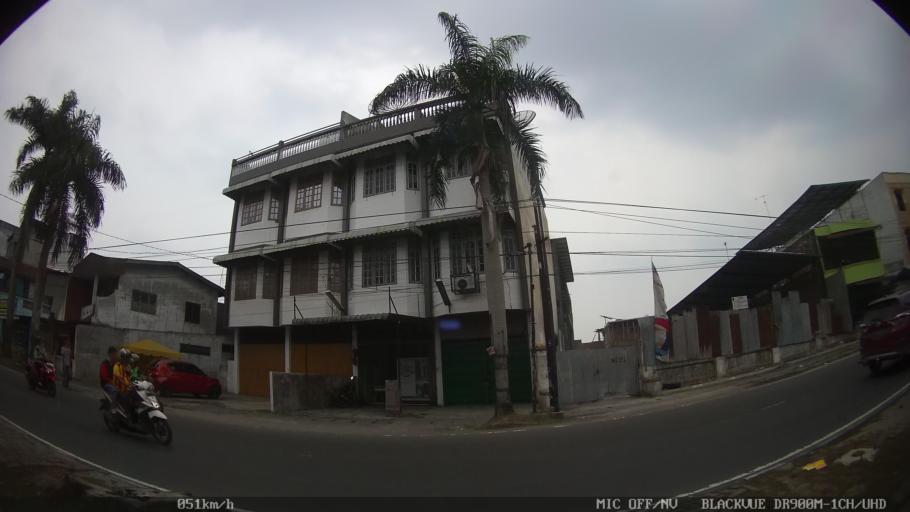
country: ID
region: North Sumatra
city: Medan
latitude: 3.5674
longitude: 98.6877
